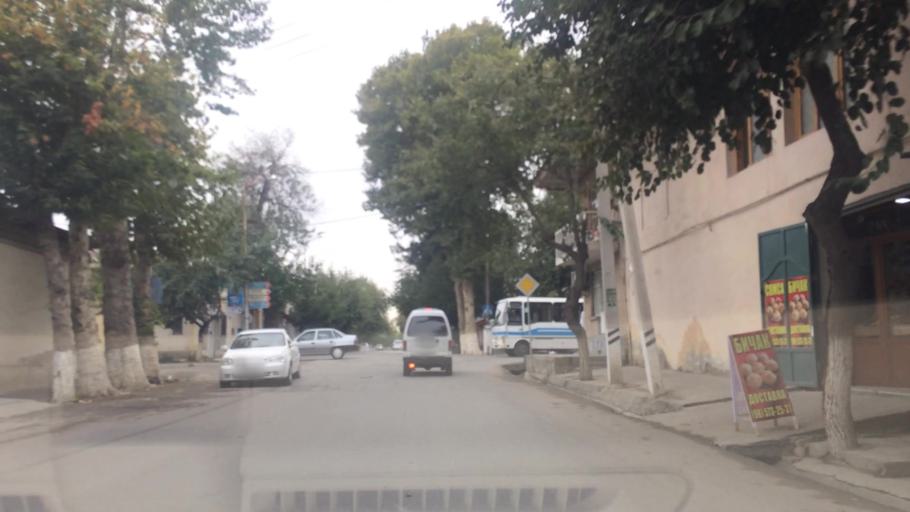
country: UZ
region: Samarqand
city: Samarqand
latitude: 39.6616
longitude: 66.9758
